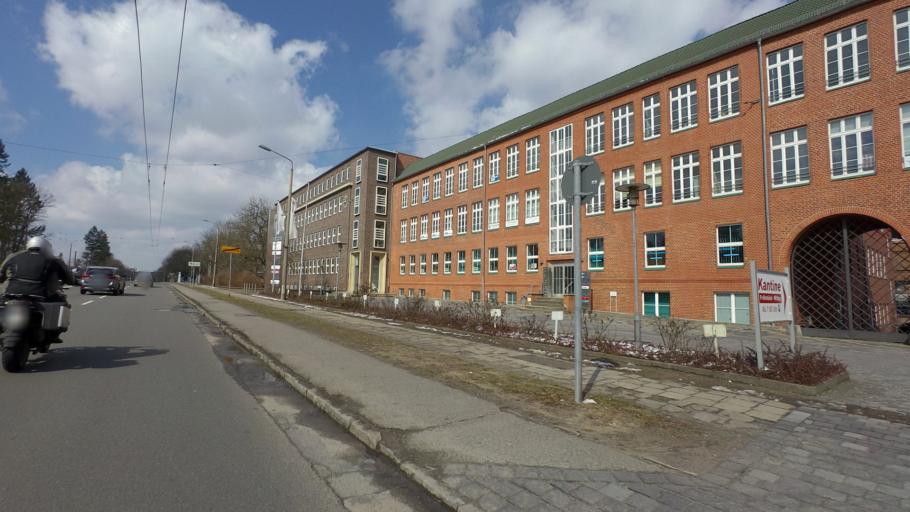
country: DE
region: Brandenburg
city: Eberswalde
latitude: 52.8382
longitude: 13.7810
